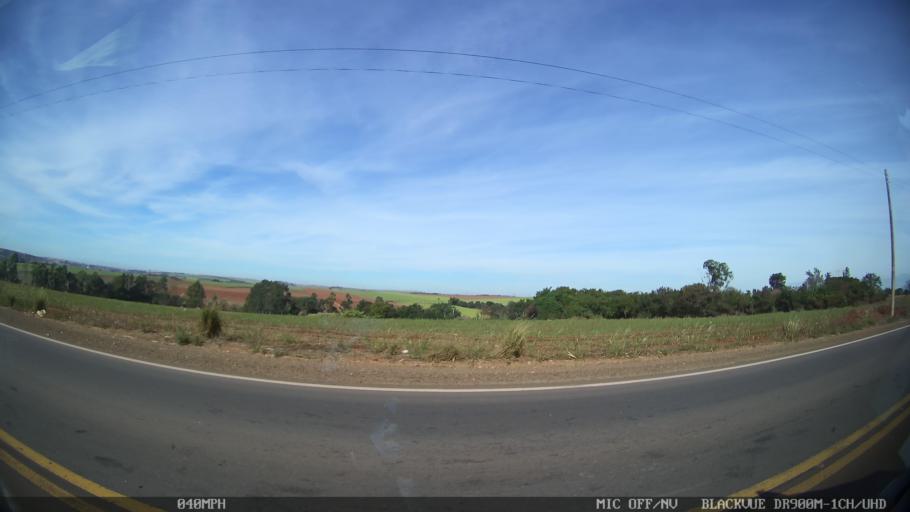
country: BR
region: Sao Paulo
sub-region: Piracicaba
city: Piracicaba
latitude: -22.7898
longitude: -47.6443
